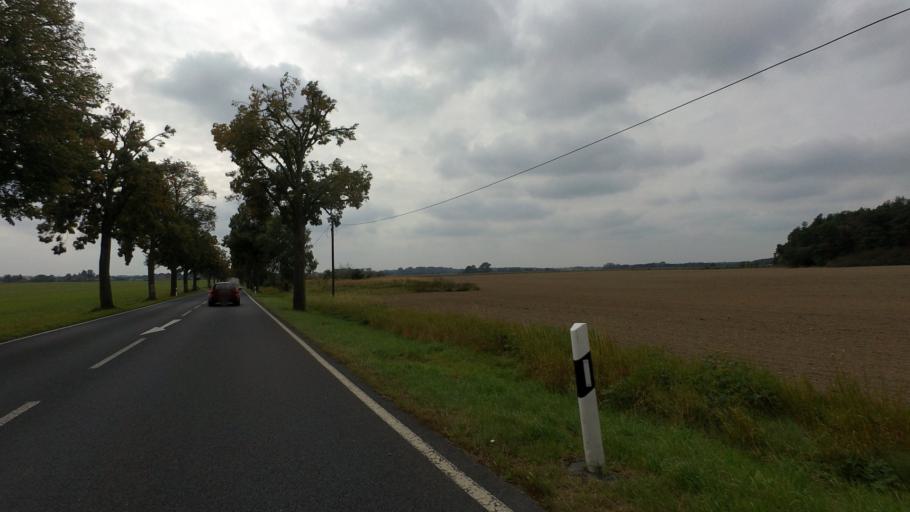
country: DE
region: Brandenburg
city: Sonnewalde
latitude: 51.7176
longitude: 13.6713
